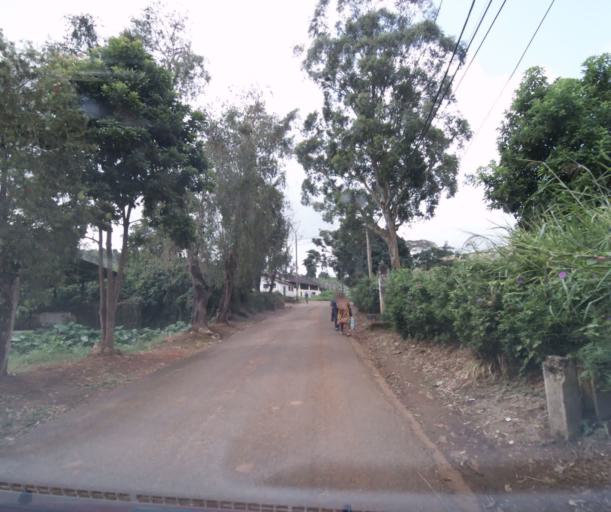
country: CM
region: West
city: Dschang
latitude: 5.4410
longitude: 10.0646
